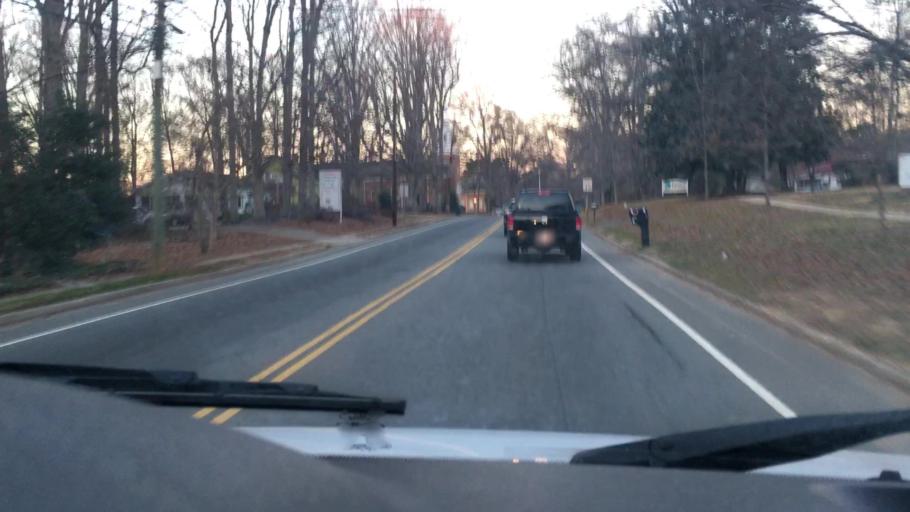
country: US
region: North Carolina
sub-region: Mecklenburg County
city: Huntersville
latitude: 35.4129
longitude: -80.8431
